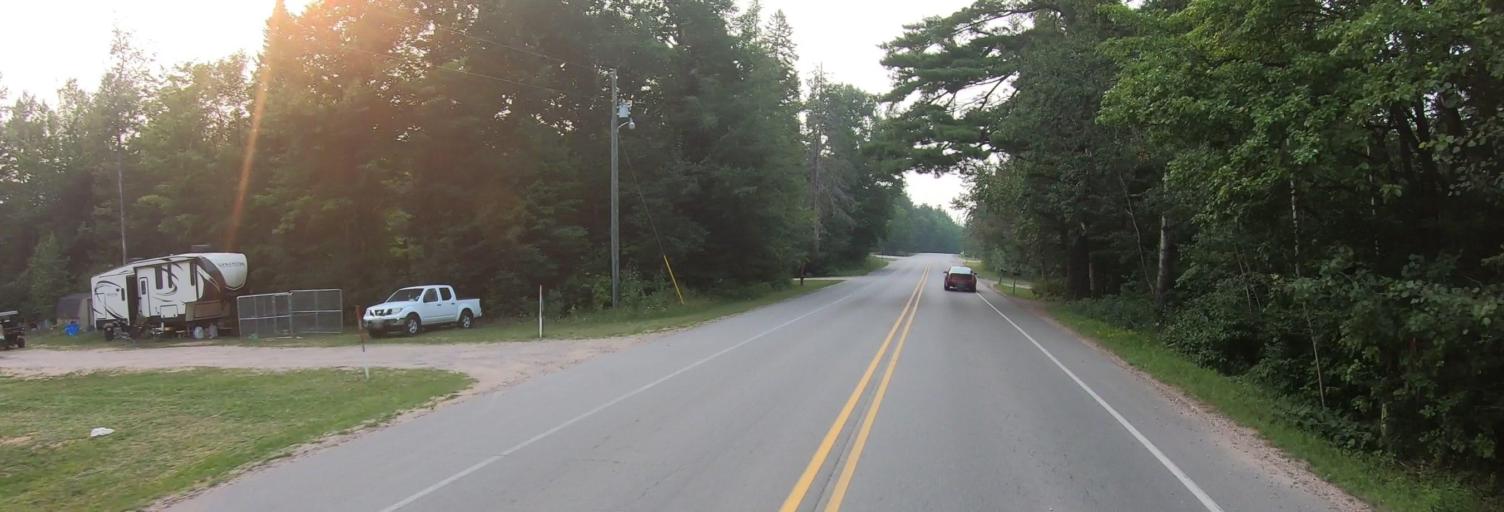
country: US
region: Michigan
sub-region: Chippewa County
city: Sault Ste. Marie
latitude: 46.4555
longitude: -84.6121
